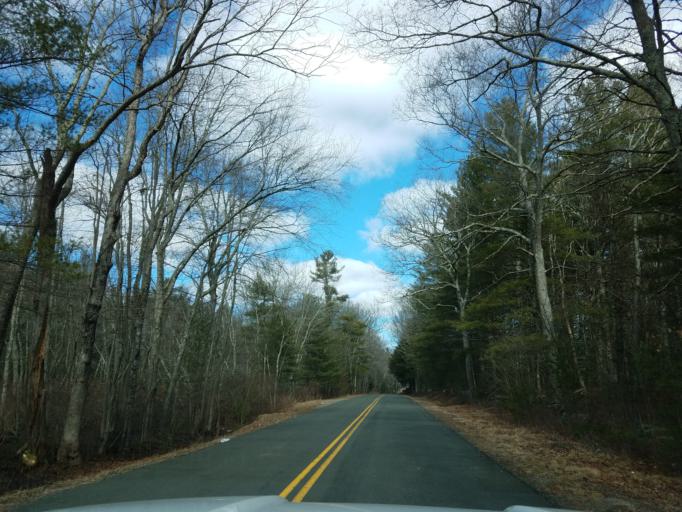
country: US
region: Massachusetts
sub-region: Worcester County
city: Dudley
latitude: 42.0182
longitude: -71.9146
